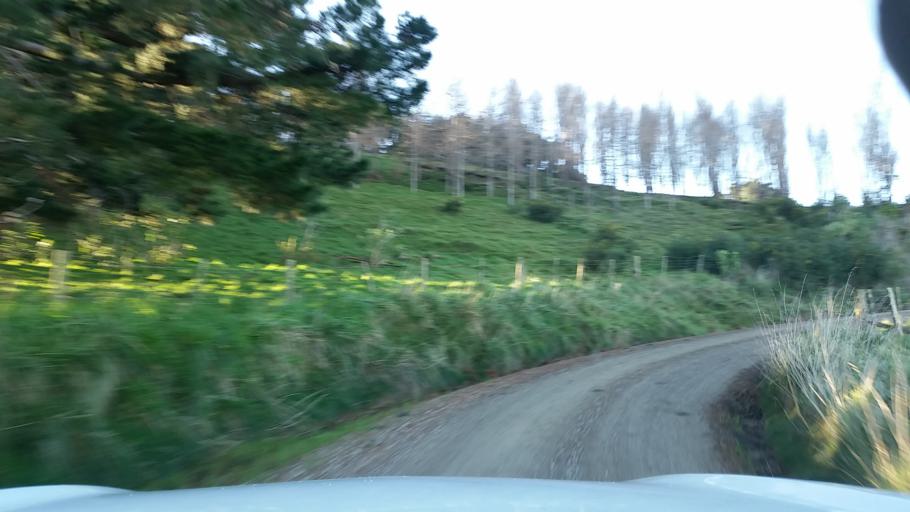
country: NZ
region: Taranaki
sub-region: South Taranaki District
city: Patea
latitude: -39.7548
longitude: 174.7466
